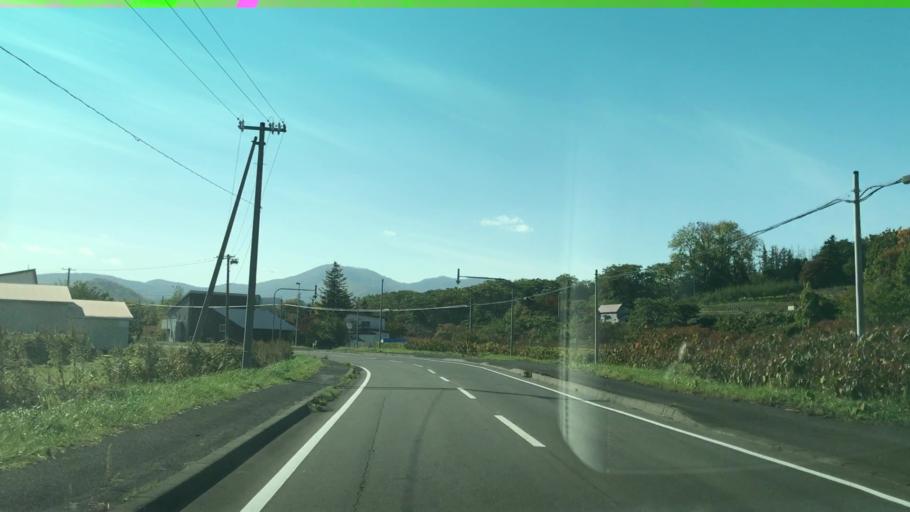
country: JP
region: Hokkaido
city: Yoichi
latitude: 43.1696
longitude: 140.8209
